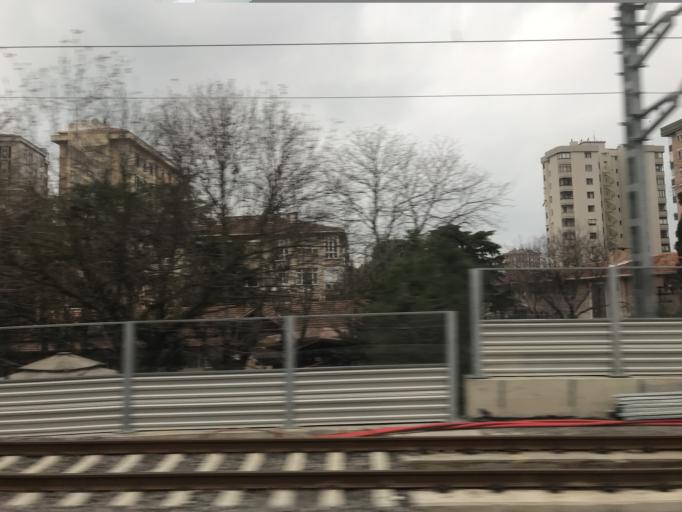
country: TR
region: Istanbul
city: UEskuedar
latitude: 40.9836
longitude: 29.0426
